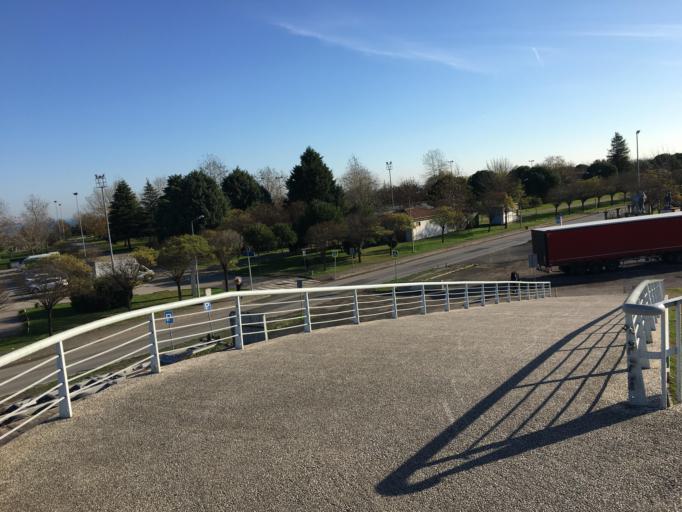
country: TR
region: Samsun
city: Samsun
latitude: 41.2849
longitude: 36.3449
